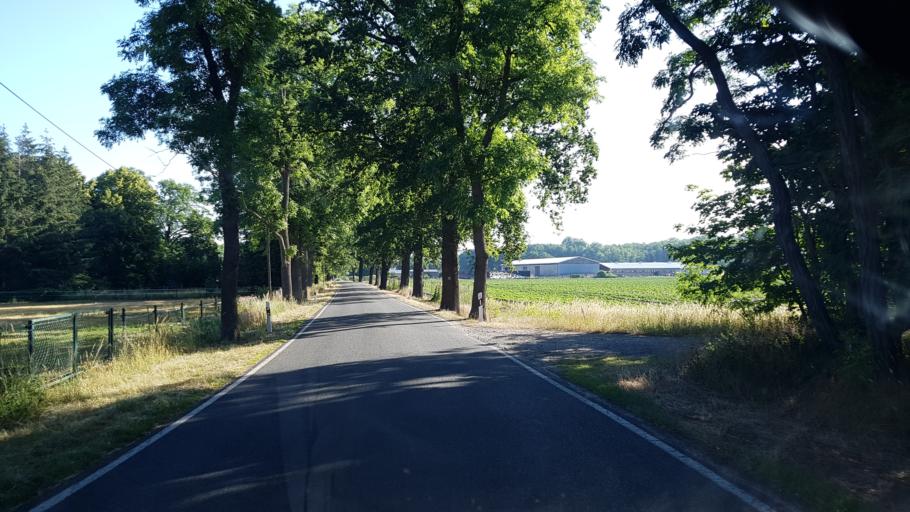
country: DE
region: Brandenburg
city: Kasel-Golzig
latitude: 51.9752
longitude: 13.6896
